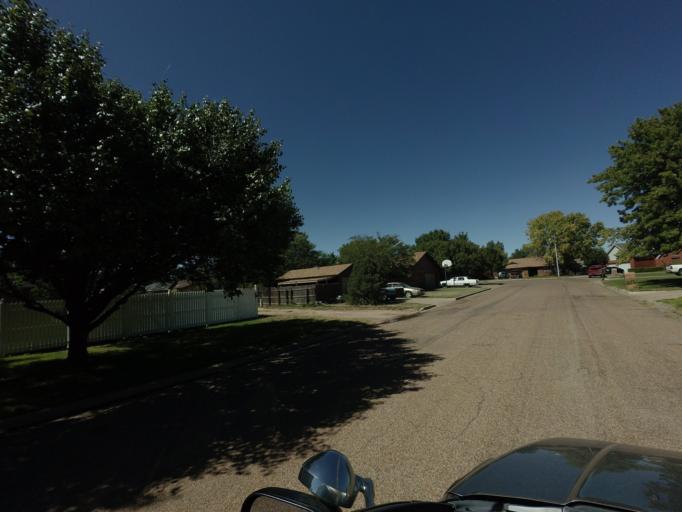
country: US
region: New Mexico
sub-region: Curry County
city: Clovis
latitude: 34.4425
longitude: -103.1792
